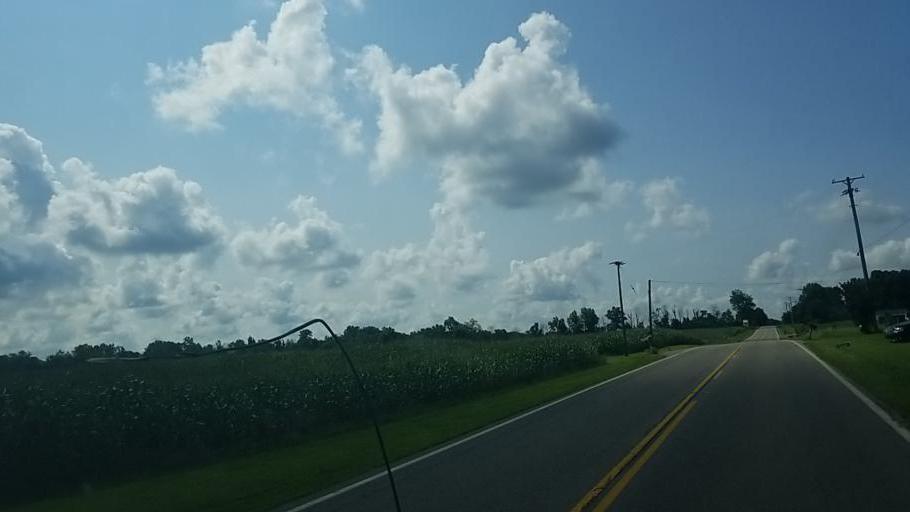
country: US
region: Ohio
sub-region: Ashland County
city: Ashland
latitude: 40.7663
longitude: -82.3068
